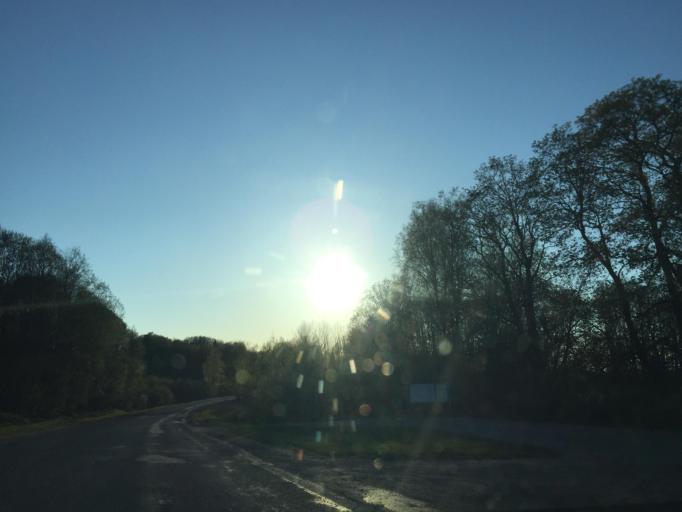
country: LV
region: Ergli
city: Ergli
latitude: 56.8757
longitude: 25.6964
